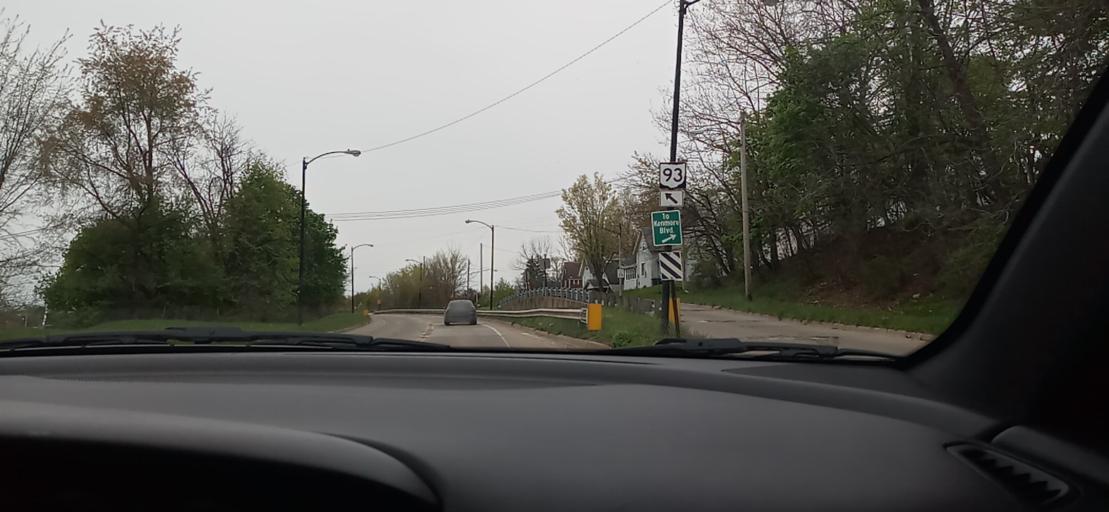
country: US
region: Ohio
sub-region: Summit County
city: Akron
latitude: 41.0473
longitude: -81.5478
